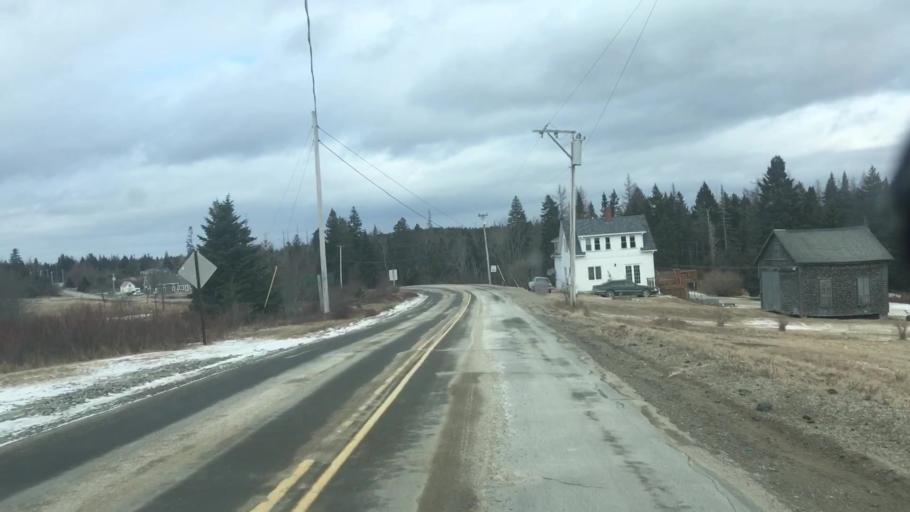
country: US
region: Maine
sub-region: Washington County
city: Machias
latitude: 44.6140
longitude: -67.4797
